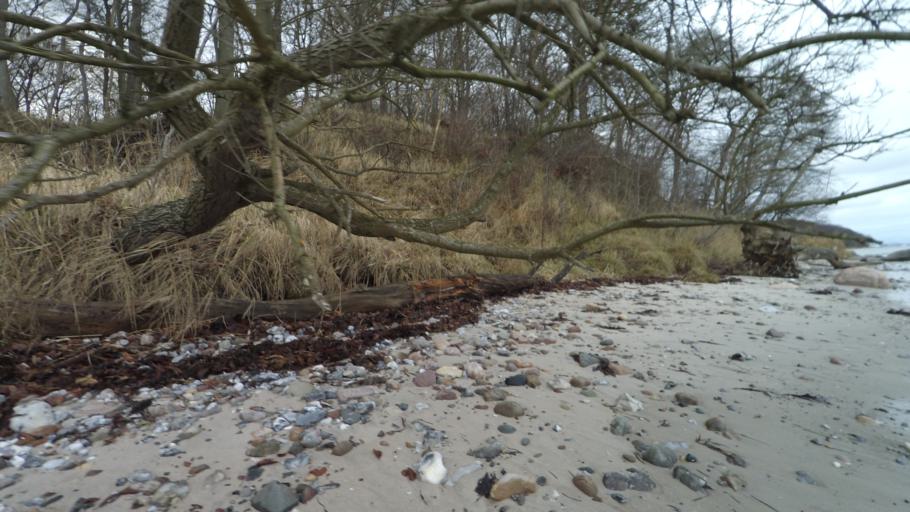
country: DK
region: Central Jutland
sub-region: Arhus Kommune
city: Beder
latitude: 56.0724
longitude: 10.2551
